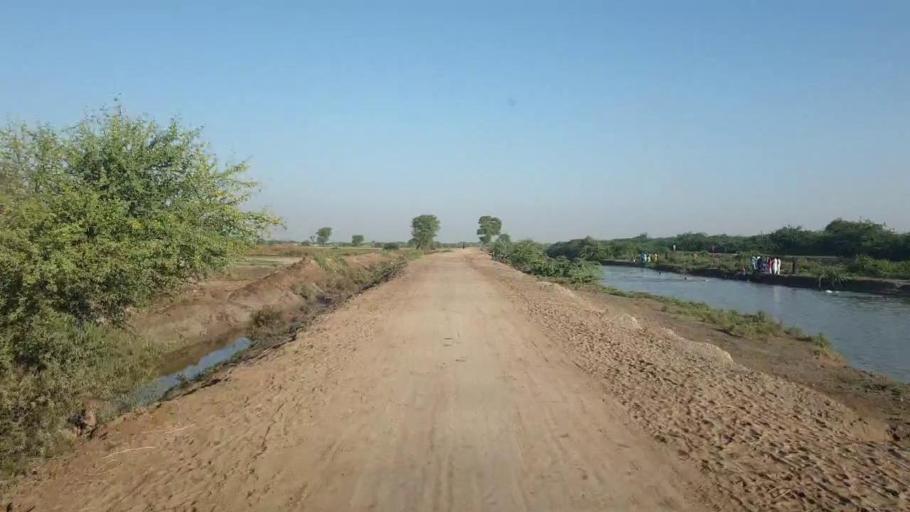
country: PK
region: Sindh
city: Badin
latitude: 24.6815
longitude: 68.8162
